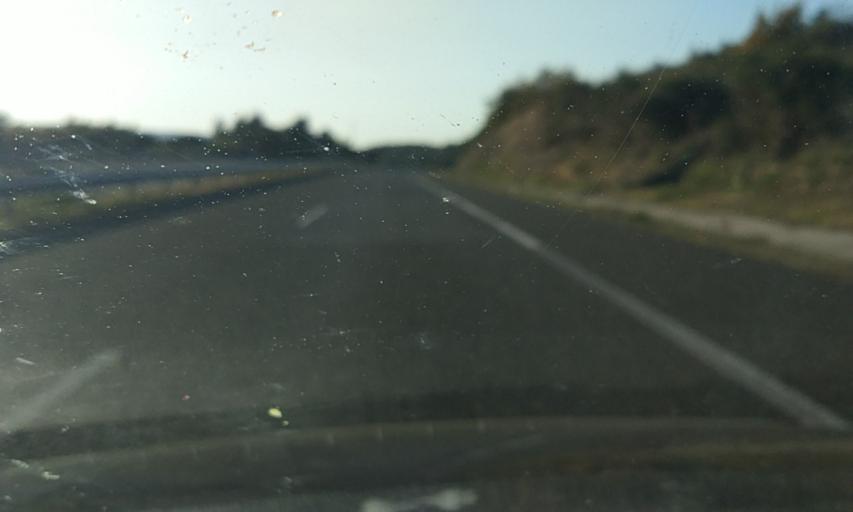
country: ES
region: Galicia
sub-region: Provincia de Ourense
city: Oimbra
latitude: 41.8537
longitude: -7.4174
